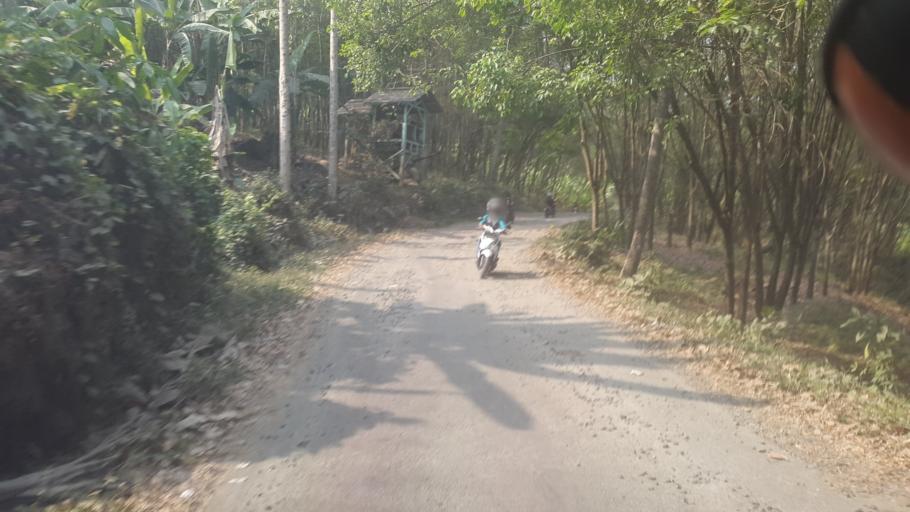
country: ID
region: West Java
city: Pelabuhanratu
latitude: -6.9603
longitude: 106.5297
